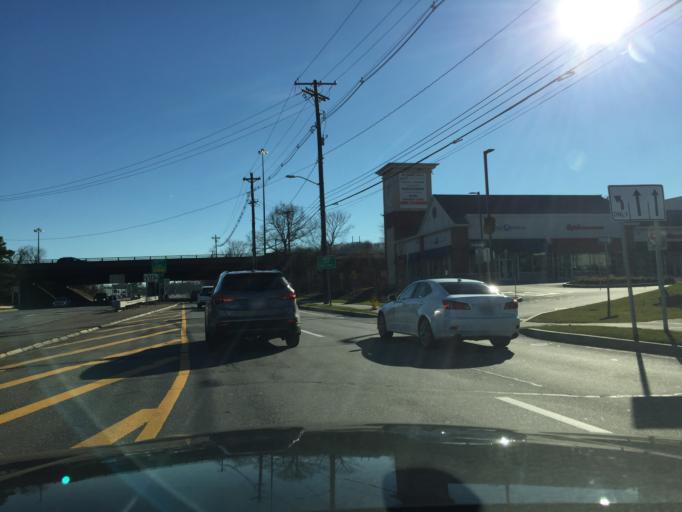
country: US
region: Massachusetts
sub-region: Middlesex County
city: Burlington
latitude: 42.4790
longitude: -71.2159
